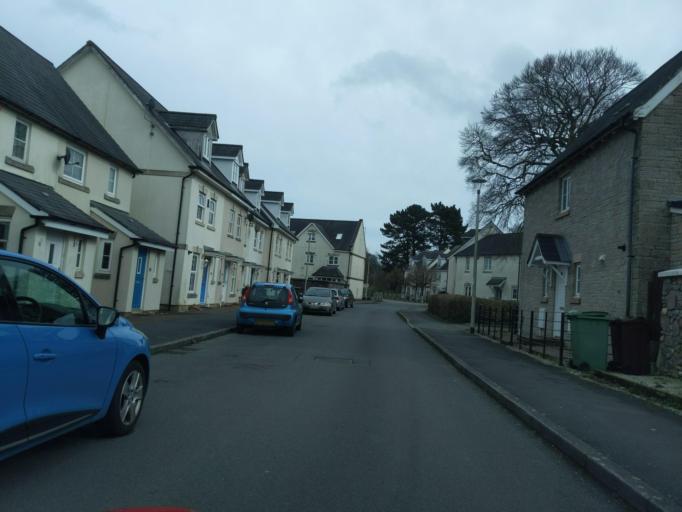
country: GB
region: England
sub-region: Plymouth
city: Plymouth
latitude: 50.4071
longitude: -4.1400
